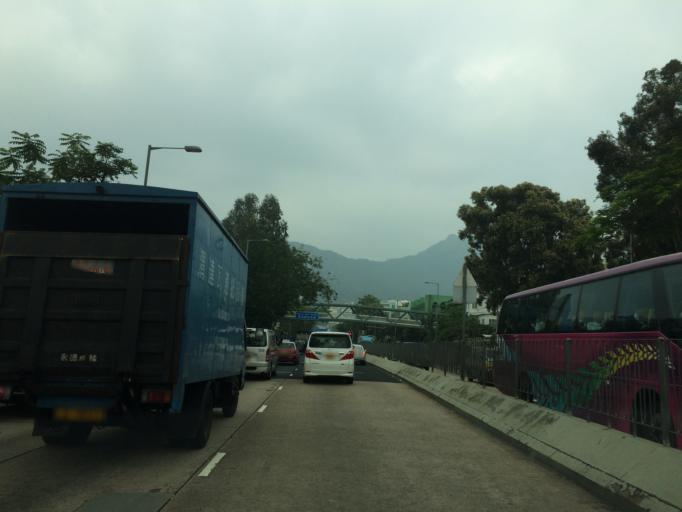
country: HK
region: Kowloon City
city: Kowloon
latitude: 22.3314
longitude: 114.1787
